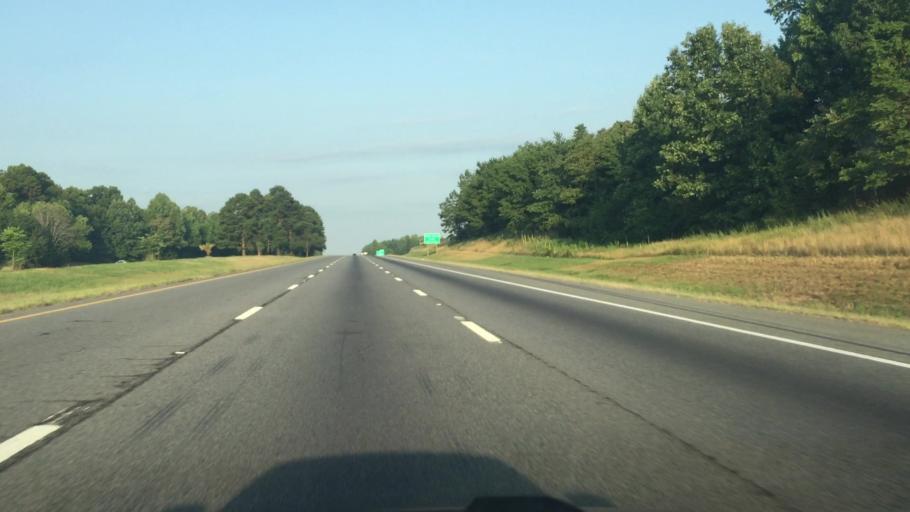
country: US
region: North Carolina
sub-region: Davidson County
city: Lexington
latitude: 35.7840
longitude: -80.2477
